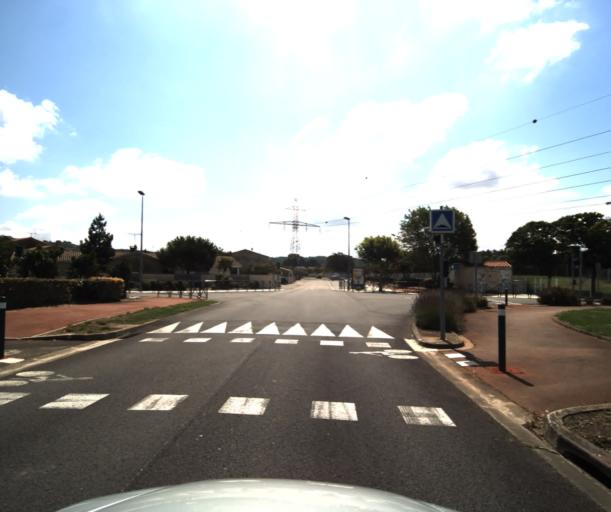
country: FR
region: Midi-Pyrenees
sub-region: Departement de la Haute-Garonne
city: Portet-sur-Garonne
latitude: 43.5321
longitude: 1.4121
